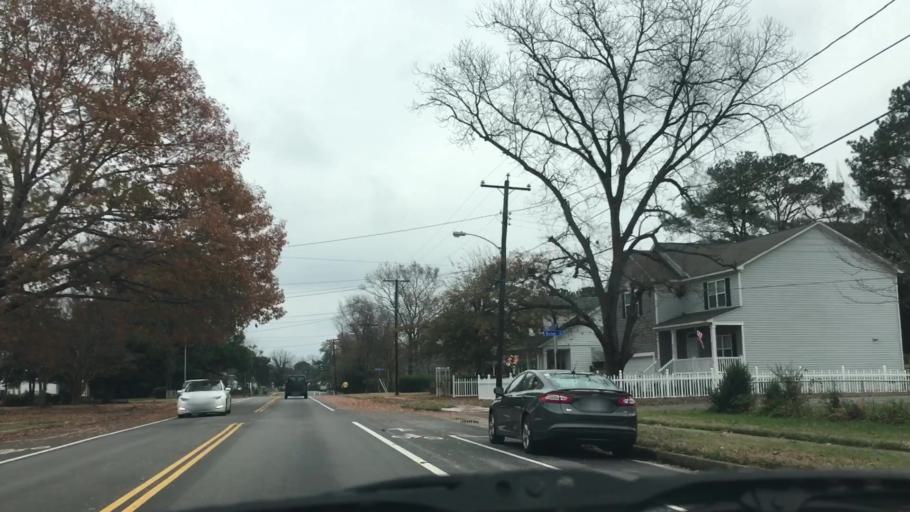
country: US
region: Virginia
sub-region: City of Norfolk
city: Norfolk
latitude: 36.8774
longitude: -76.2455
